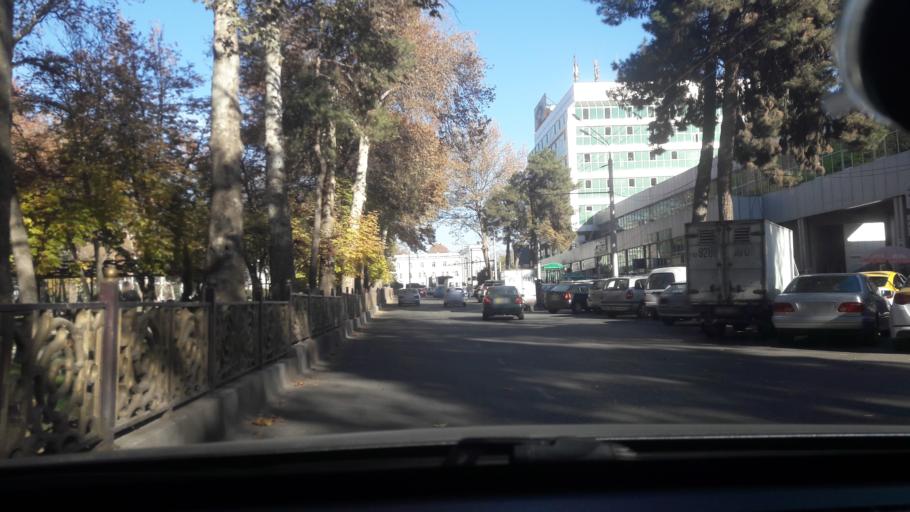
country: TJ
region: Dushanbe
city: Dushanbe
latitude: 38.5607
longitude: 68.7996
